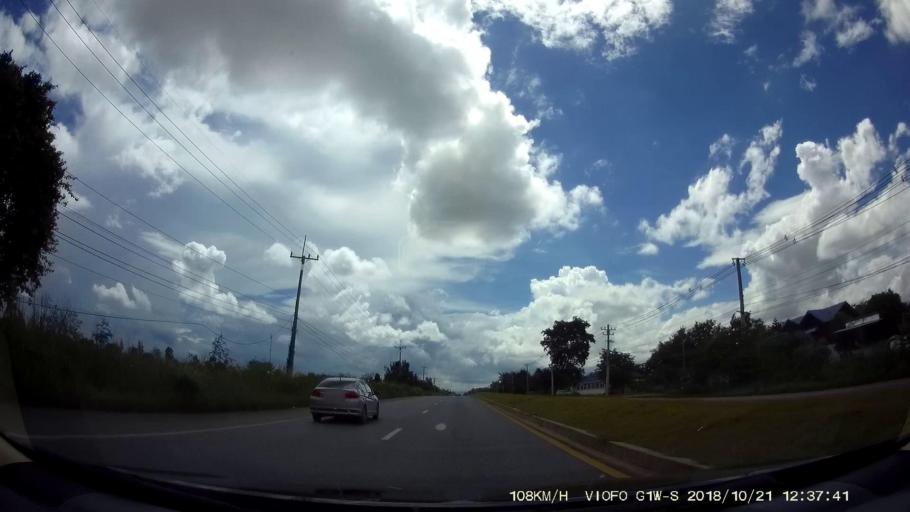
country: TH
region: Nakhon Ratchasima
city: Dan Khun Thot
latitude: 15.0653
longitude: 101.7100
